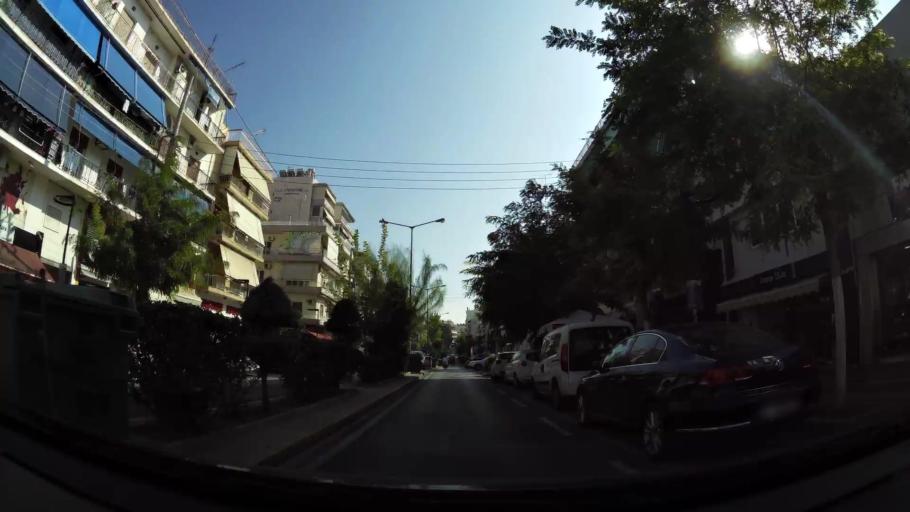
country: GR
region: Attica
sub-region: Nomos Piraios
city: Keratsini
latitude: 37.9663
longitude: 23.6230
